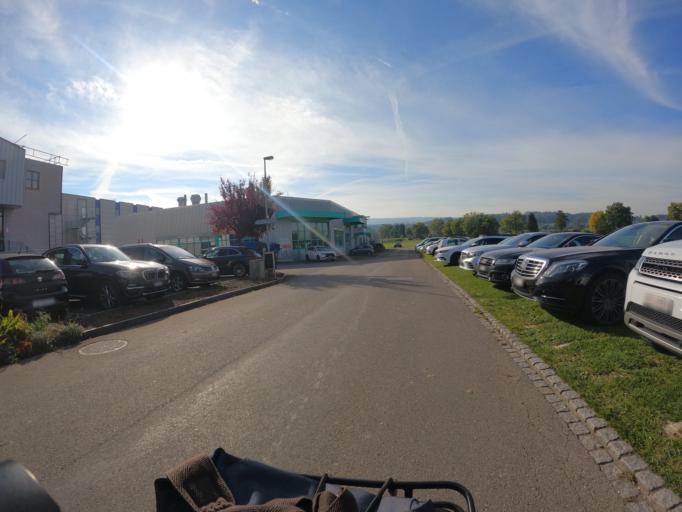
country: CH
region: Aargau
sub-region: Bezirk Muri
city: Merenschwand
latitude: 47.2621
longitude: 8.3844
